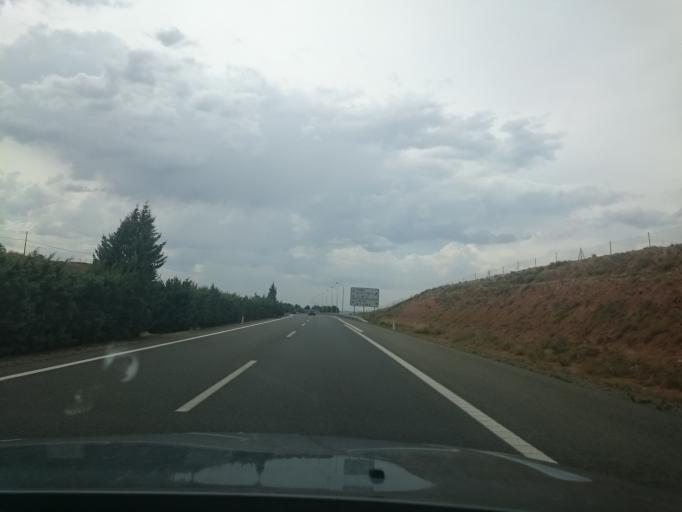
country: ES
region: Navarre
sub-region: Provincia de Navarra
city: Fontellas
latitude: 42.0100
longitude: -1.5921
